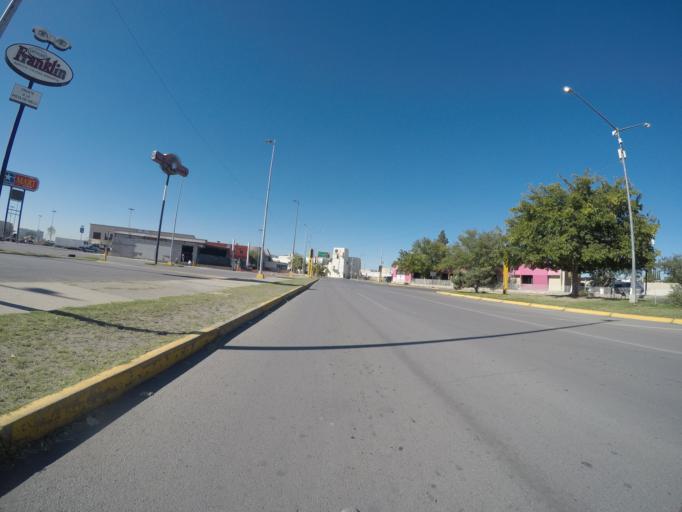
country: MX
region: Chihuahua
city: Ciudad Juarez
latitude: 31.7422
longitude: -106.4528
